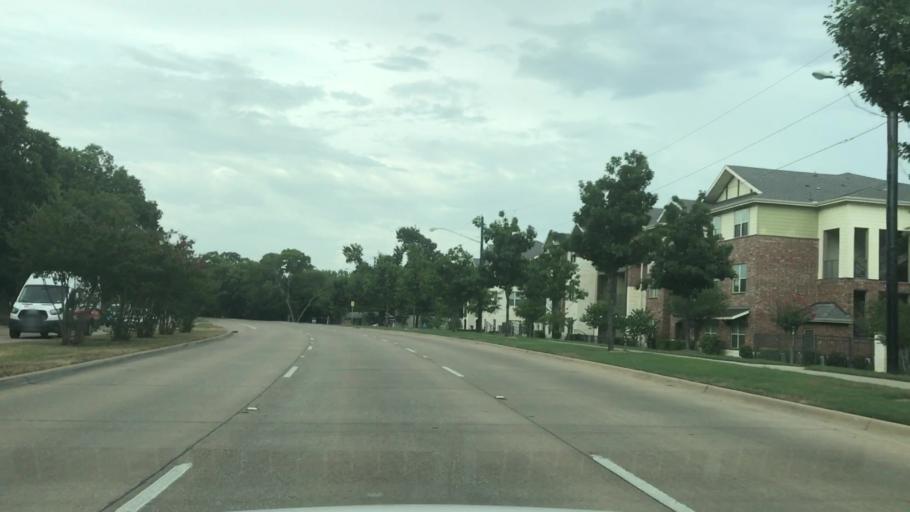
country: US
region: Texas
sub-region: Dallas County
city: Highland Park
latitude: 32.8693
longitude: -96.7364
